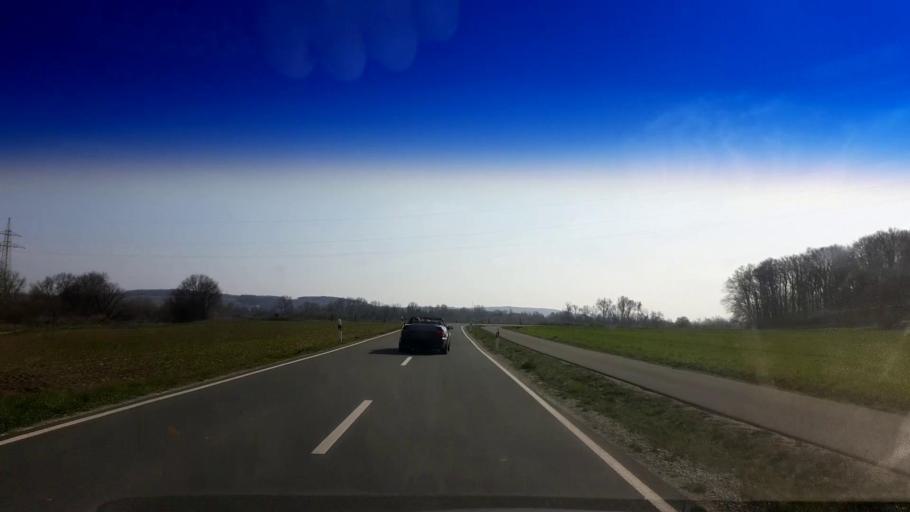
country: DE
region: Bavaria
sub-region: Upper Franconia
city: Ebensfeld
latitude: 50.0624
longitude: 10.9393
